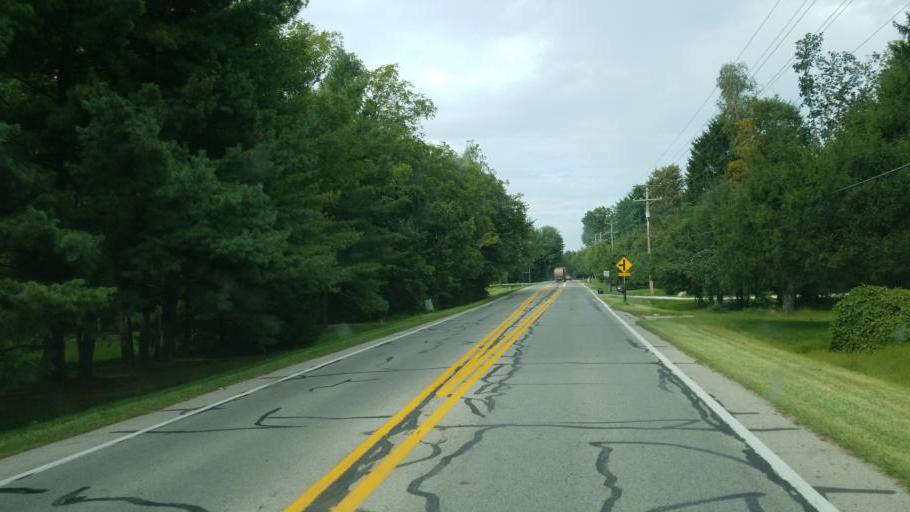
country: US
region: Ohio
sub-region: Franklin County
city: New Albany
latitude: 40.0386
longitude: -82.8108
